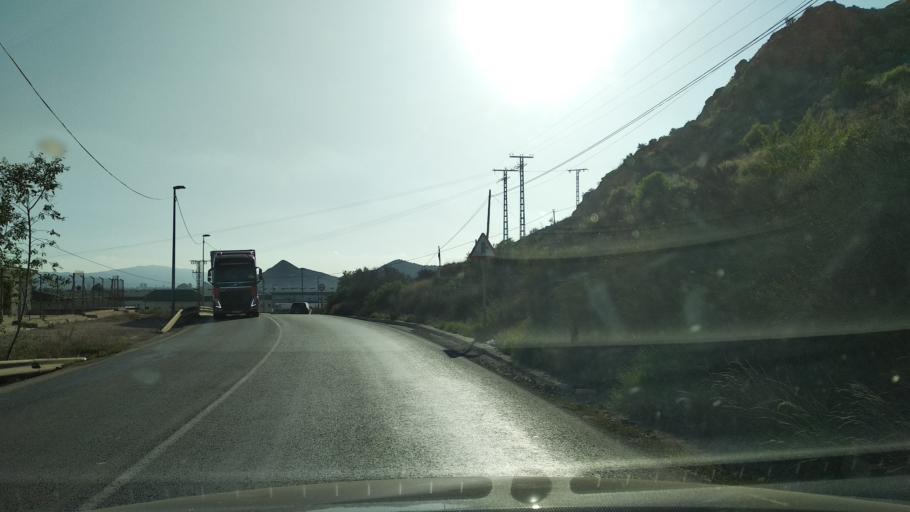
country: ES
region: Murcia
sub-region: Murcia
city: Santomera
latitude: 38.0530
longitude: -1.0552
